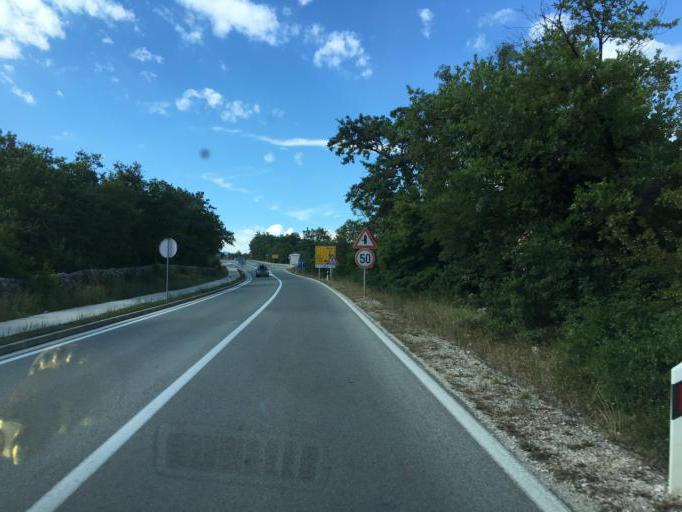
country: HR
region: Primorsko-Goranska
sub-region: Grad Krk
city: Krk
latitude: 45.0559
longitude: 14.5570
